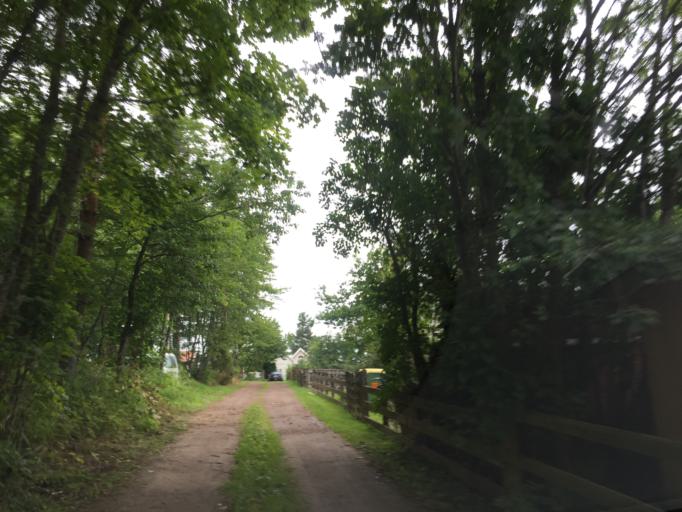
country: SE
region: OEstergoetland
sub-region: Vadstena Kommun
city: Vadstena
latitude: 58.4722
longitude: 14.8406
